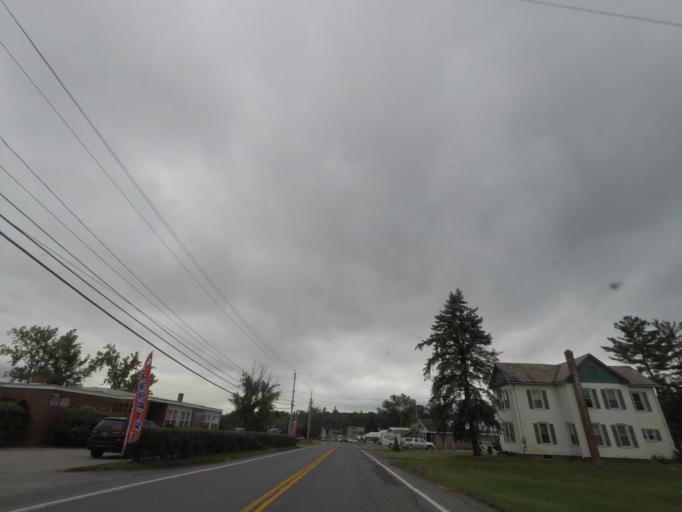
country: US
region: New York
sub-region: Rensselaer County
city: Hoosick Falls
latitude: 42.9167
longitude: -73.3510
